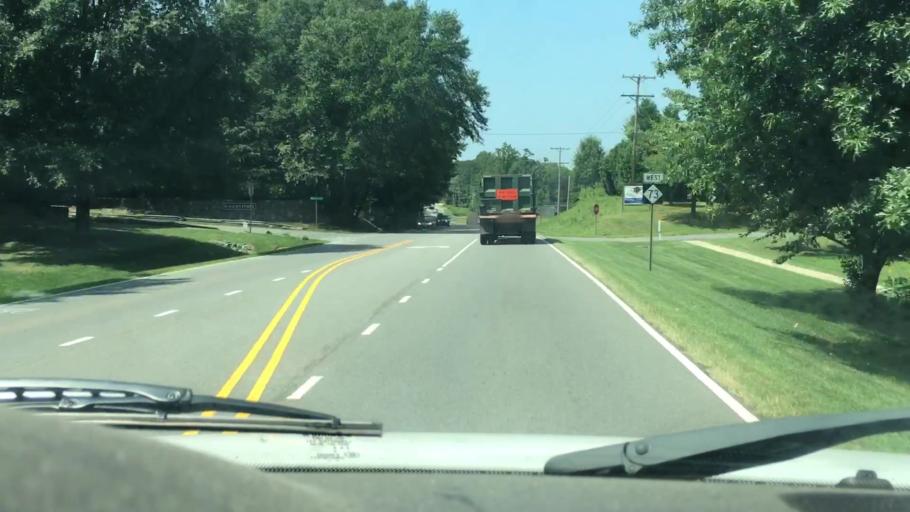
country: US
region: North Carolina
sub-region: Lincoln County
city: Lowesville
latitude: 35.4285
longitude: -80.9347
